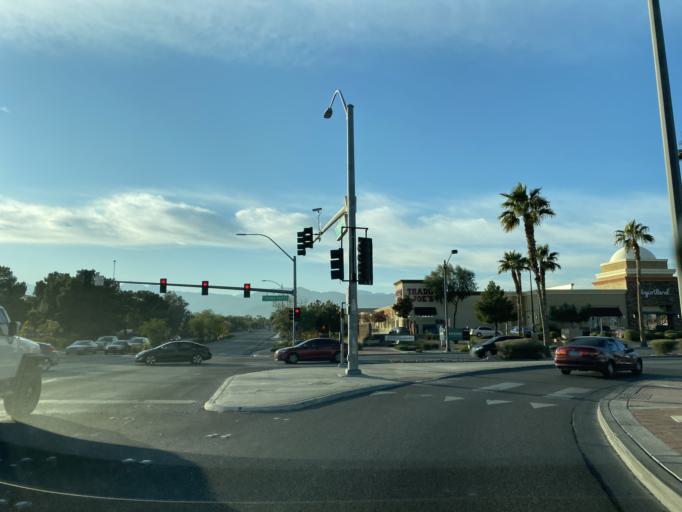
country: US
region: Nevada
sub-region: Clark County
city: Las Vegas
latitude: 36.2632
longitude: -115.2563
